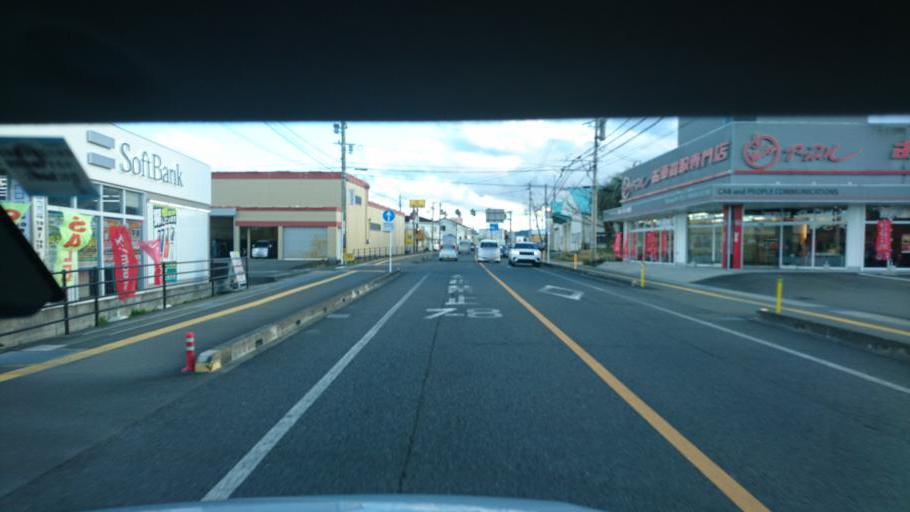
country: JP
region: Miyazaki
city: Miyazaki-shi
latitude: 31.8721
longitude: 131.4316
